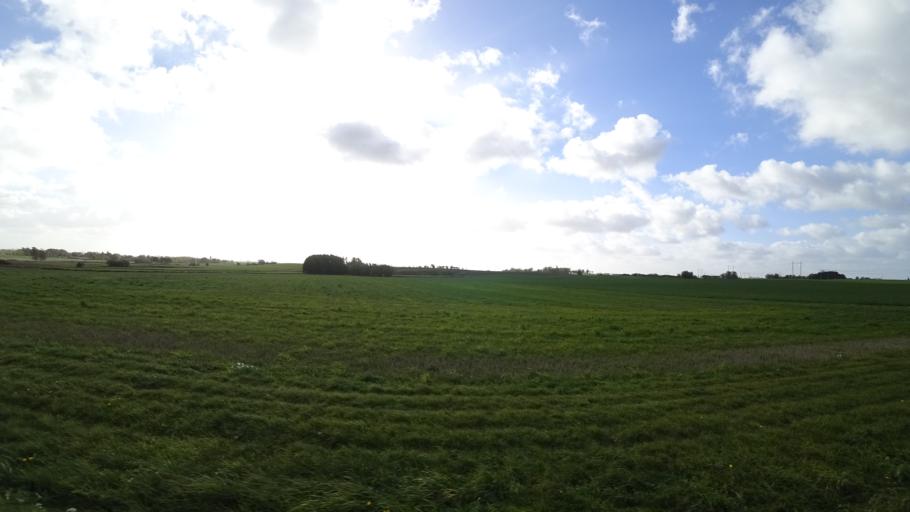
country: SE
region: Skane
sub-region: Staffanstorps Kommun
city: Hjaerup
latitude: 55.6361
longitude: 13.1615
